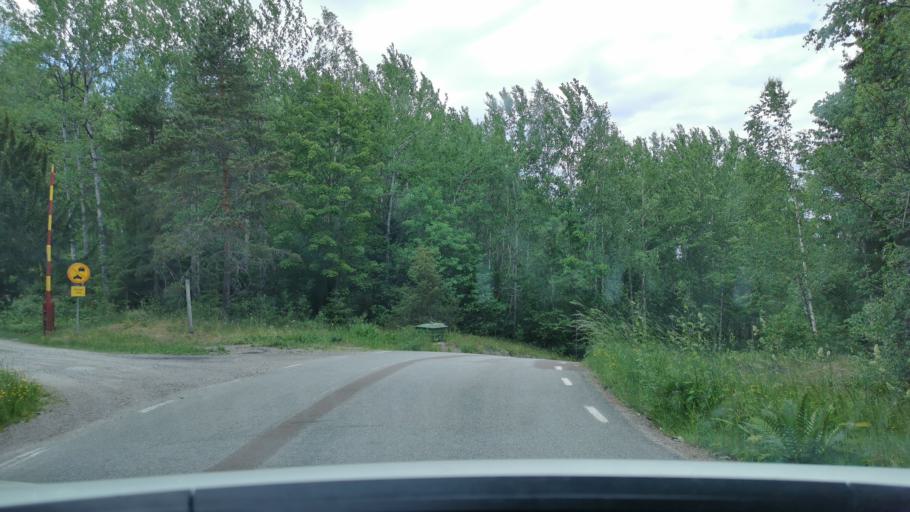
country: SE
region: Vaestra Goetaland
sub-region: Bengtsfors Kommun
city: Dals Langed
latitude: 58.8565
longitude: 12.4036
